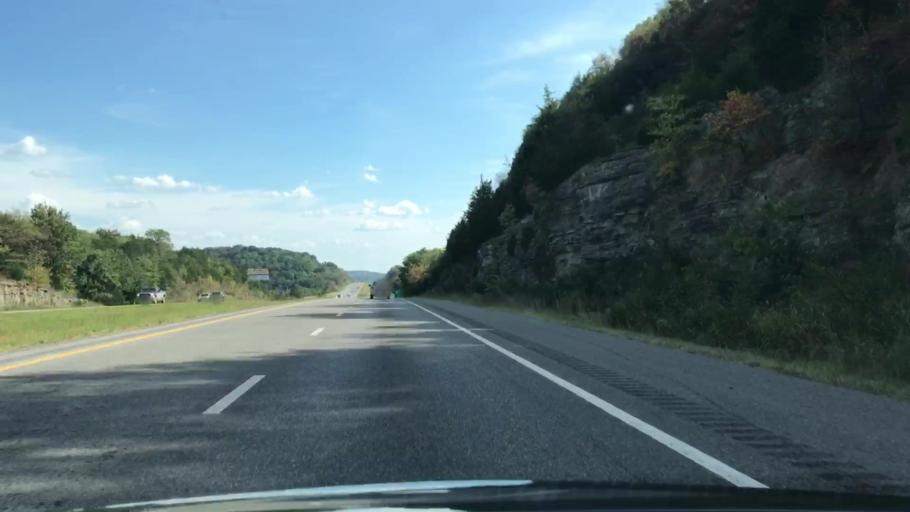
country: US
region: Alabama
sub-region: Limestone County
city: Ardmore
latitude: 35.0890
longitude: -86.8845
